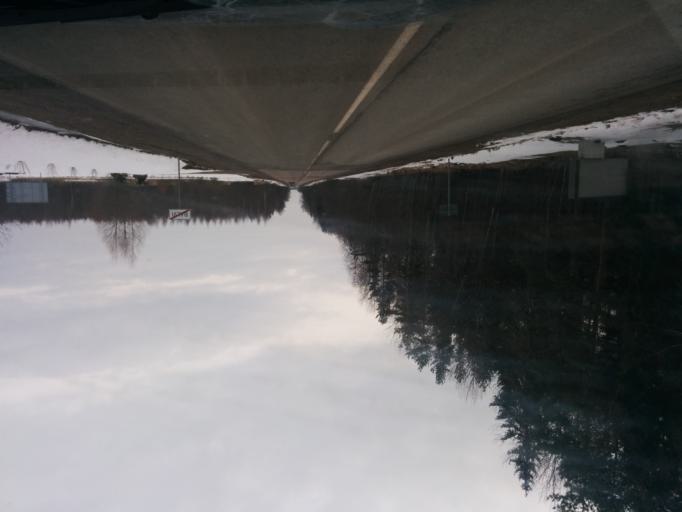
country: LV
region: Balvu Rajons
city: Balvi
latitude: 57.1429
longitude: 27.2430
